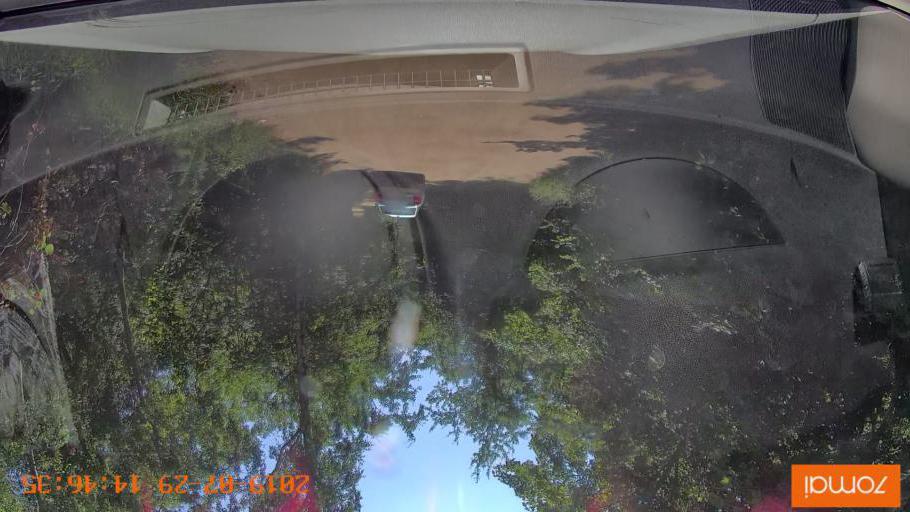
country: RU
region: Kaliningrad
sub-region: Gorod Kaliningrad
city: Baltiysk
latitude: 54.6639
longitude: 19.9022
